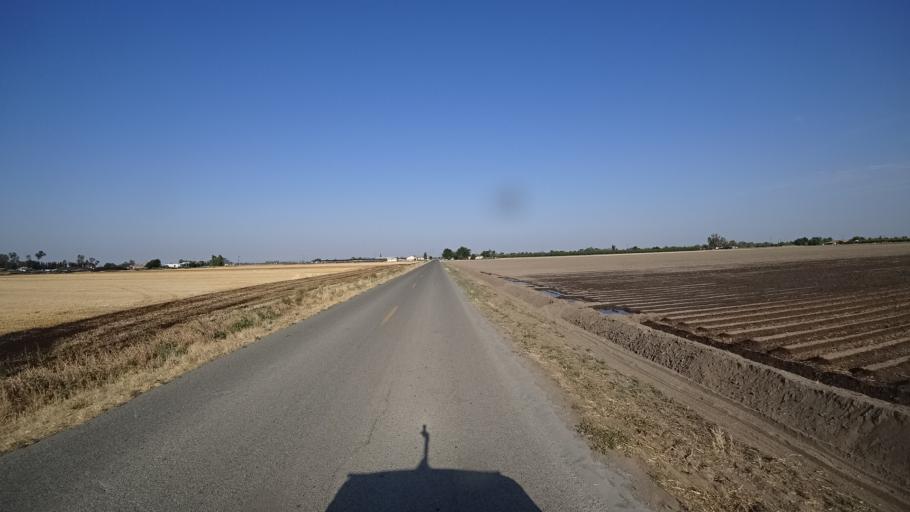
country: US
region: California
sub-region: Fresno County
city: Riverdale
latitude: 36.3803
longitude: -119.8390
